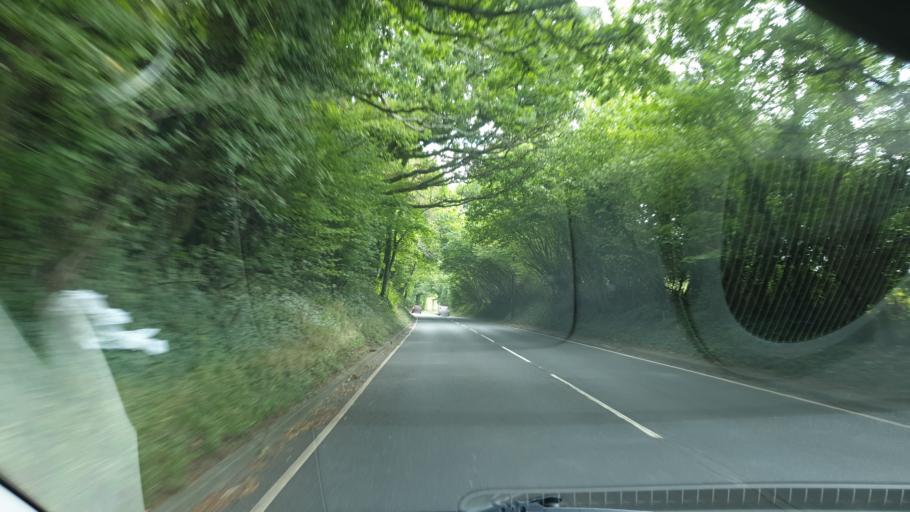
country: GB
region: England
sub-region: East Sussex
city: Forest Row
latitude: 51.1046
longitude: 0.0267
